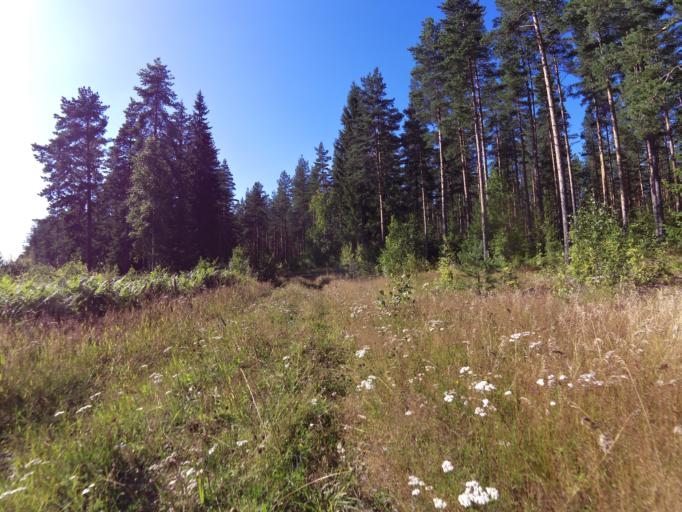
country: SE
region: Gaevleborg
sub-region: Hofors Kommun
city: Hofors
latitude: 60.5704
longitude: 16.4581
